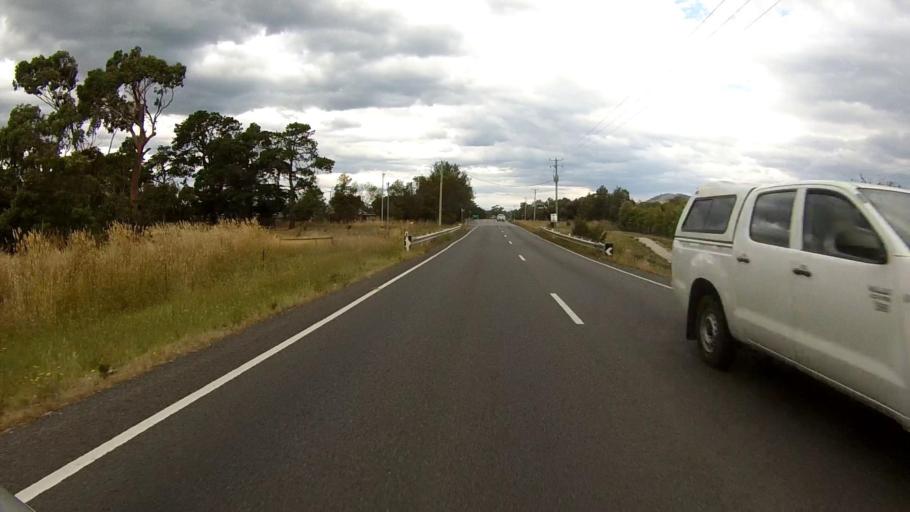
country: AU
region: Tasmania
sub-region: Clarence
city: Cambridge
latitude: -42.8424
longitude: 147.4722
